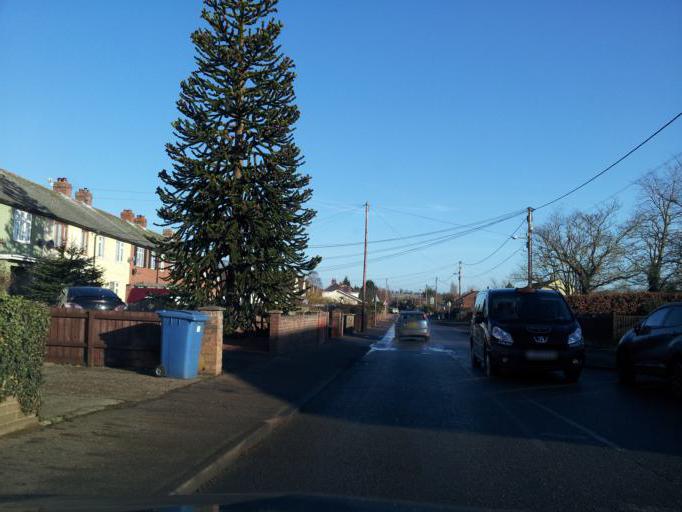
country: GB
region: England
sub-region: Suffolk
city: Sudbury
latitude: 52.0264
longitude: 0.7475
